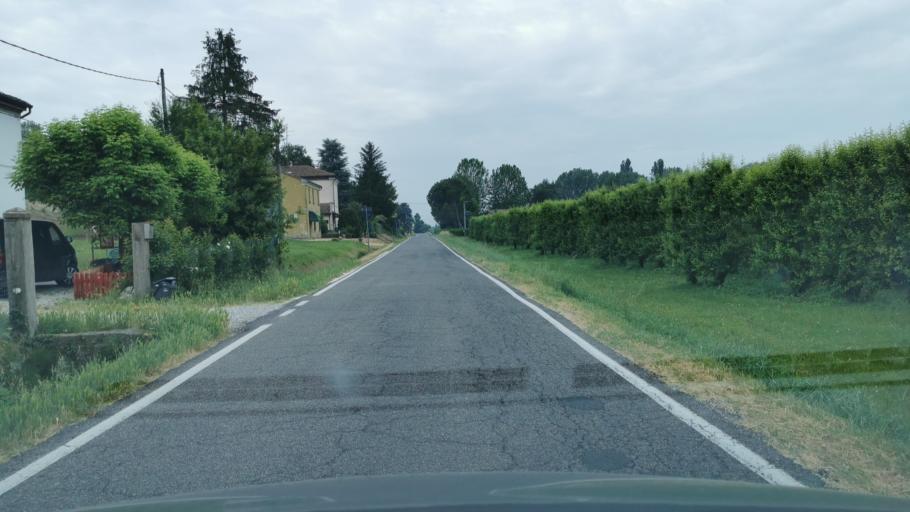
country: IT
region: Emilia-Romagna
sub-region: Provincia di Ravenna
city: Russi
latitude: 44.4007
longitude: 12.0213
